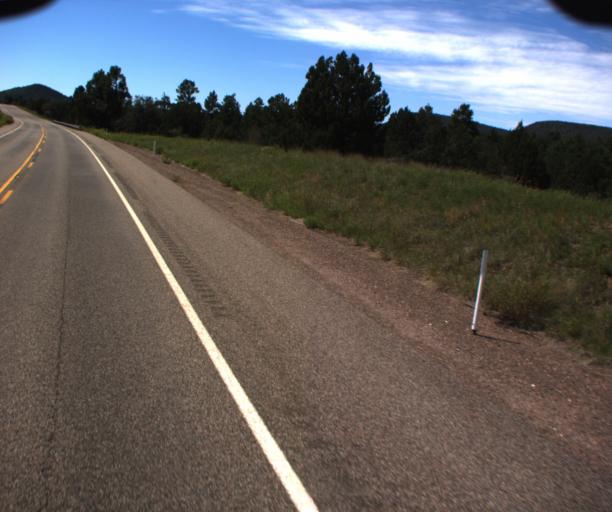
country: US
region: Arizona
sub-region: Gila County
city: San Carlos
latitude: 33.6796
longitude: -110.5729
